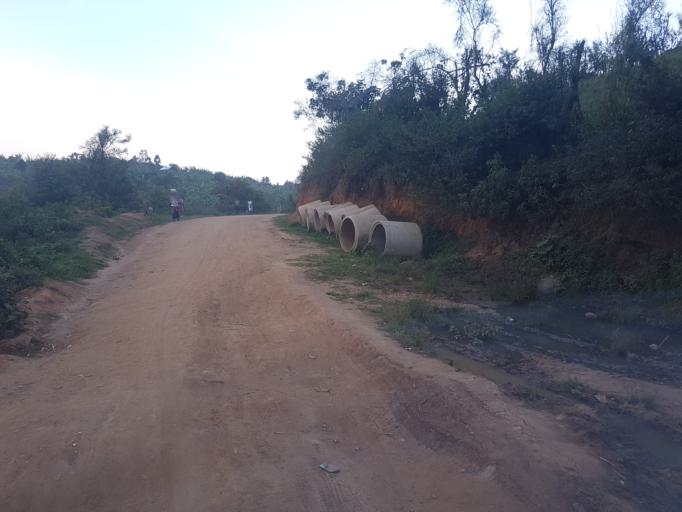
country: UG
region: Western Region
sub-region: Mitoma District
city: Mitoma
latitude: -0.6784
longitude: 29.9362
